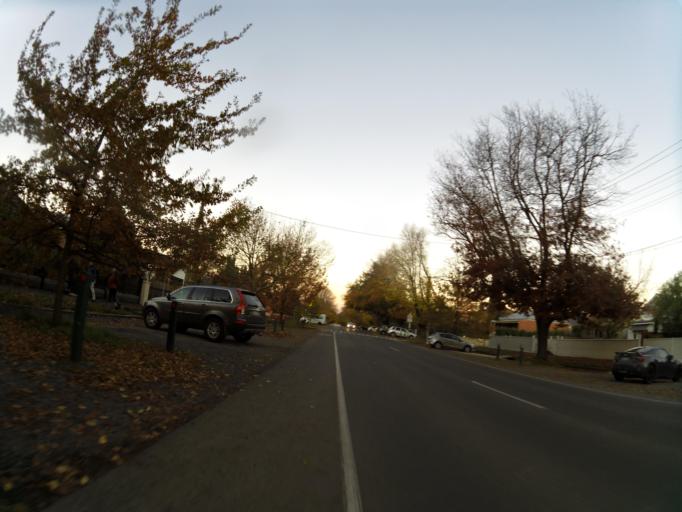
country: AU
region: Victoria
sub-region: Ballarat North
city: Ballarat Central
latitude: -37.5567
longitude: 143.8500
